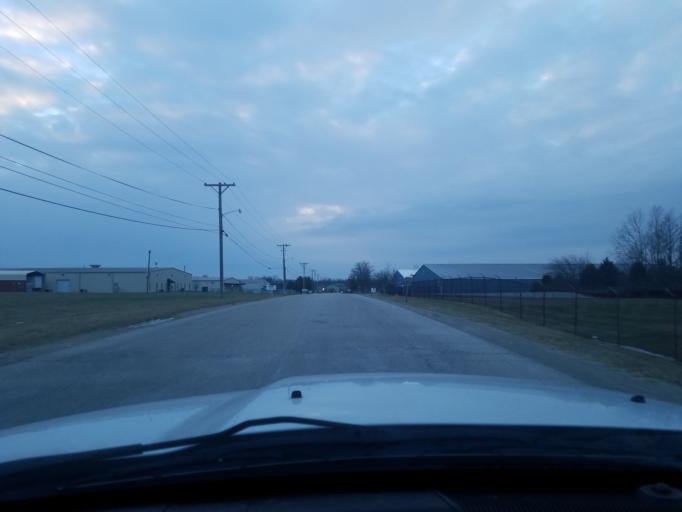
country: US
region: Kentucky
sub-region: Oldham County
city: Buckner
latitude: 38.3753
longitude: -85.4440
